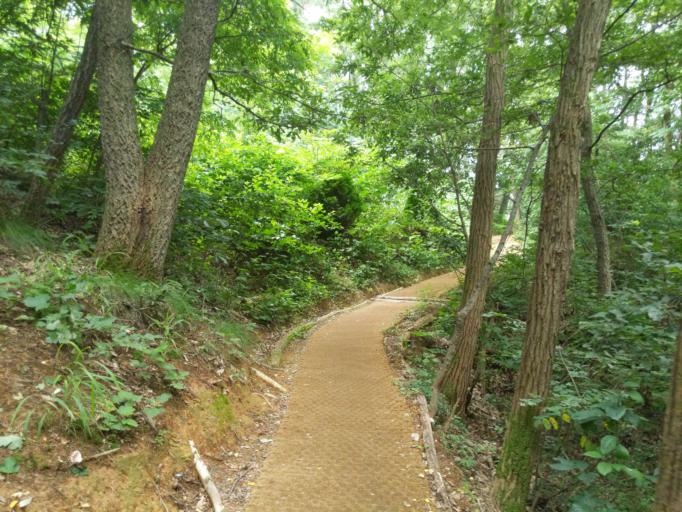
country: KR
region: Daegu
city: Hwawon
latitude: 35.7926
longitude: 128.5245
